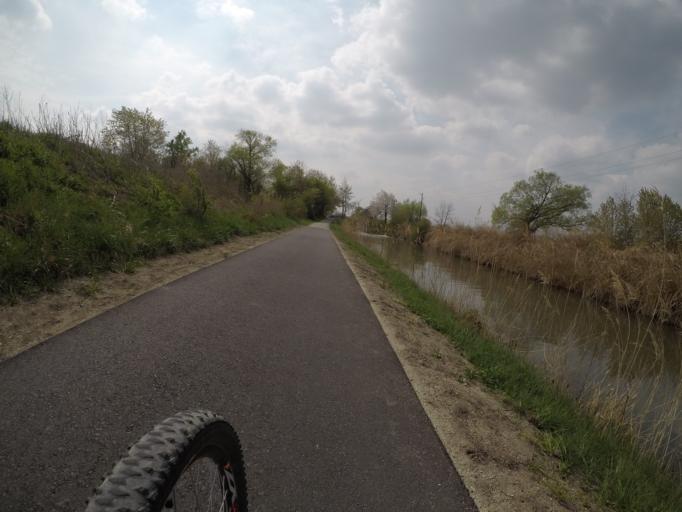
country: AT
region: Lower Austria
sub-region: Politischer Bezirk Baden
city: Traiskirchen
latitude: 48.0231
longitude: 16.2790
